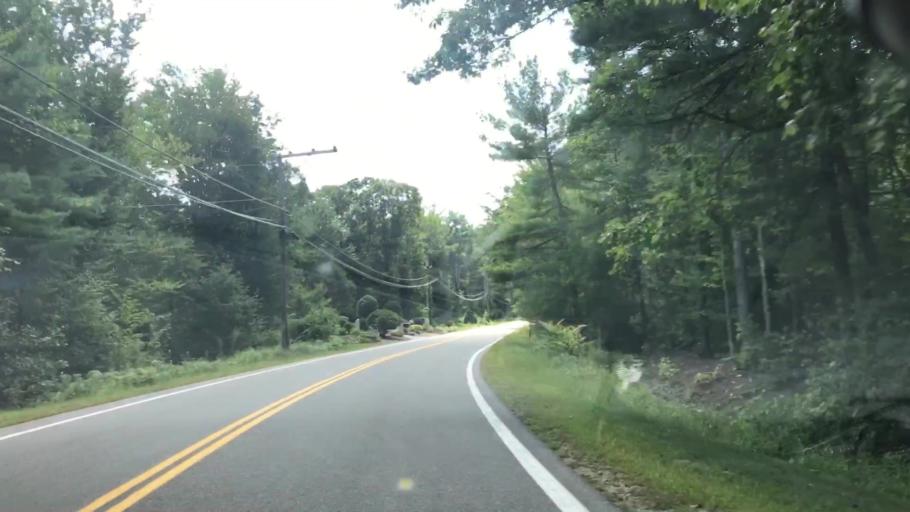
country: US
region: New Hampshire
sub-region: Hillsborough County
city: Bedford
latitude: 42.9318
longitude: -71.5514
